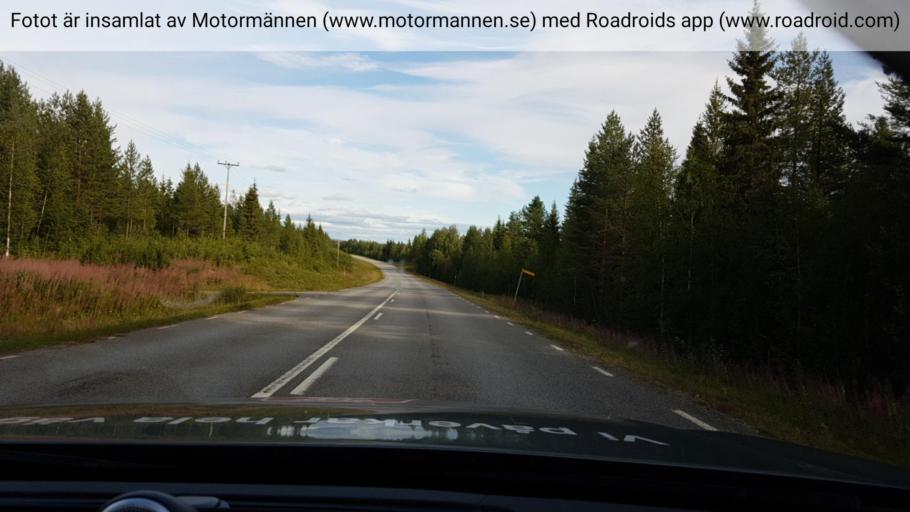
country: SE
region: Jaemtland
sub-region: Stroemsunds Kommun
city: Stroemsund
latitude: 64.2512
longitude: 15.4209
